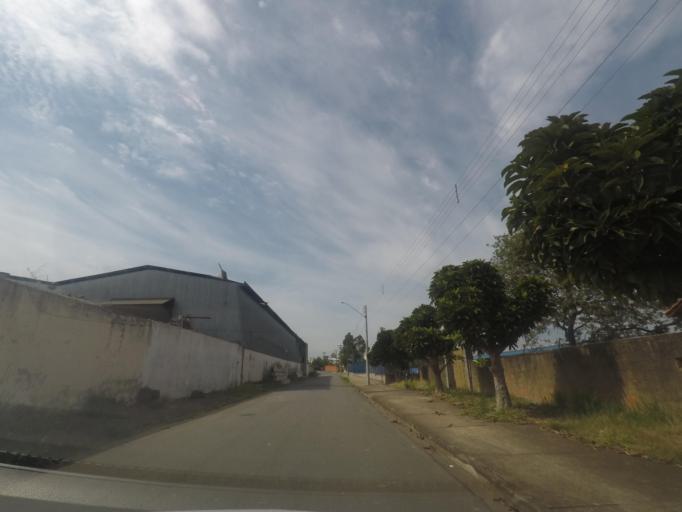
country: BR
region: Sao Paulo
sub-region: Sumare
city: Sumare
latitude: -22.8032
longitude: -47.2472
